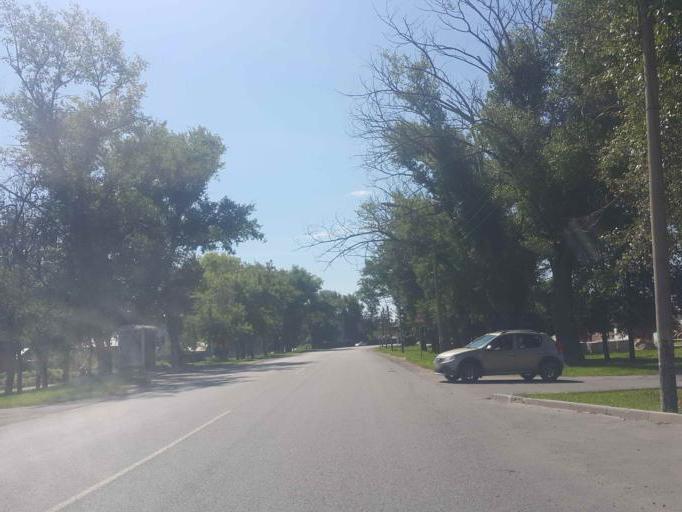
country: RU
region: Tambov
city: Pokrovo-Prigorodnoye
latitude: 52.7119
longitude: 41.4200
